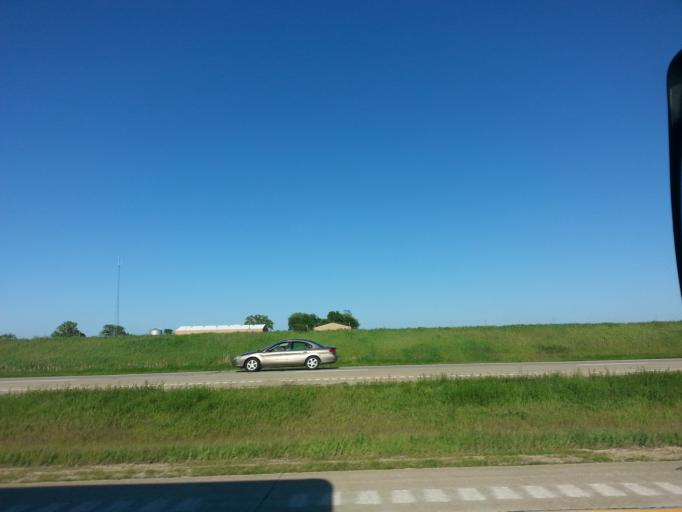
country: US
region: Illinois
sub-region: Woodford County
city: El Paso
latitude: 40.7602
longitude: -89.0347
